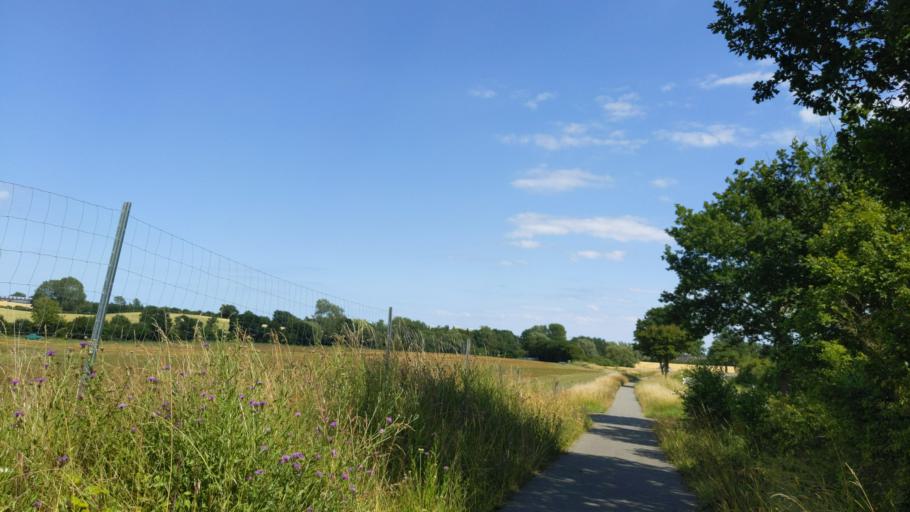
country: DE
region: Schleswig-Holstein
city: Gromitz
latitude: 54.1556
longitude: 10.9348
